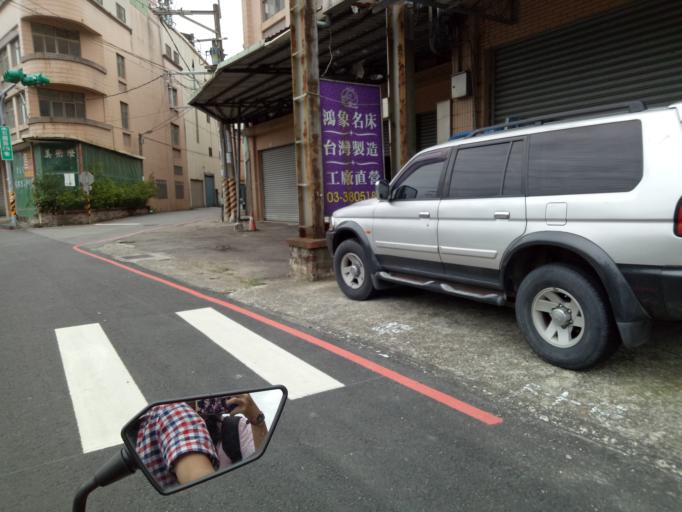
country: TW
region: Taiwan
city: Daxi
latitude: 24.8752
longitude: 121.2629
